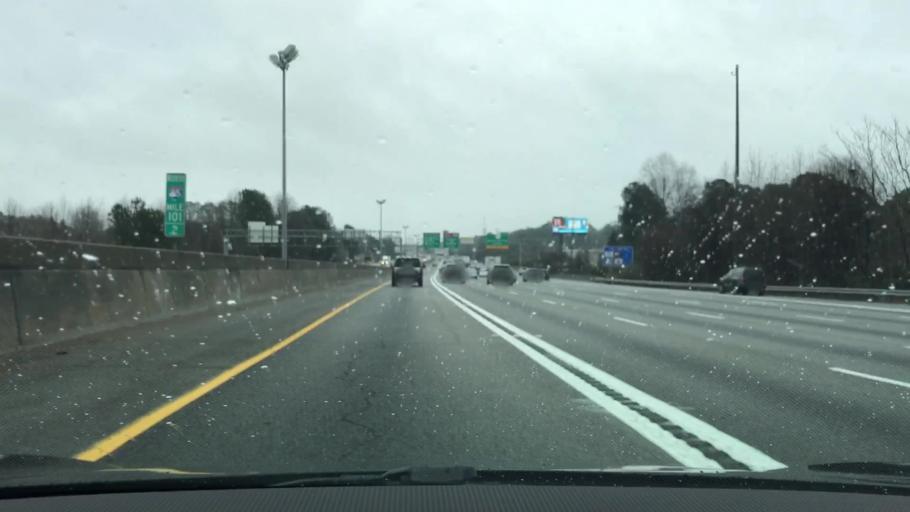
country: US
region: Georgia
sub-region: Gwinnett County
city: Norcross
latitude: 33.9299
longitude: -84.1719
